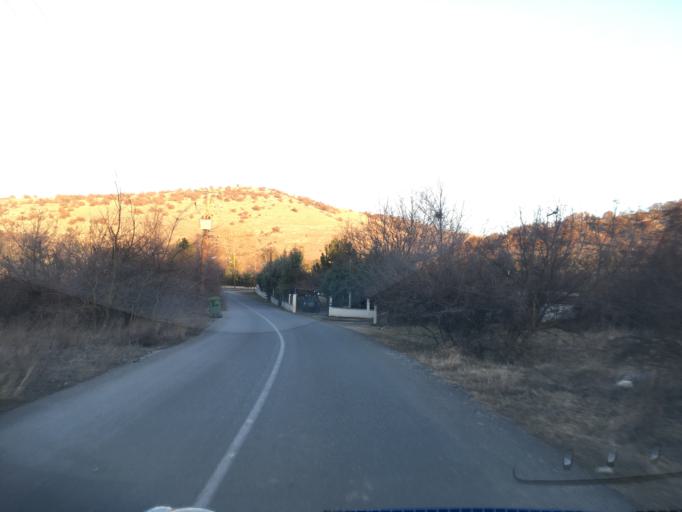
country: GR
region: West Macedonia
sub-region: Nomos Kozanis
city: Koila
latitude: 40.3285
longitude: 21.8068
